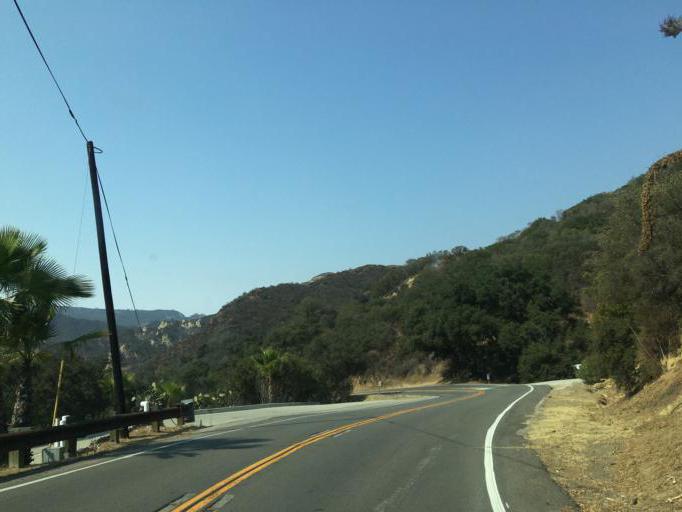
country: US
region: California
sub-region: Los Angeles County
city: Calabasas
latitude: 34.1214
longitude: -118.6314
